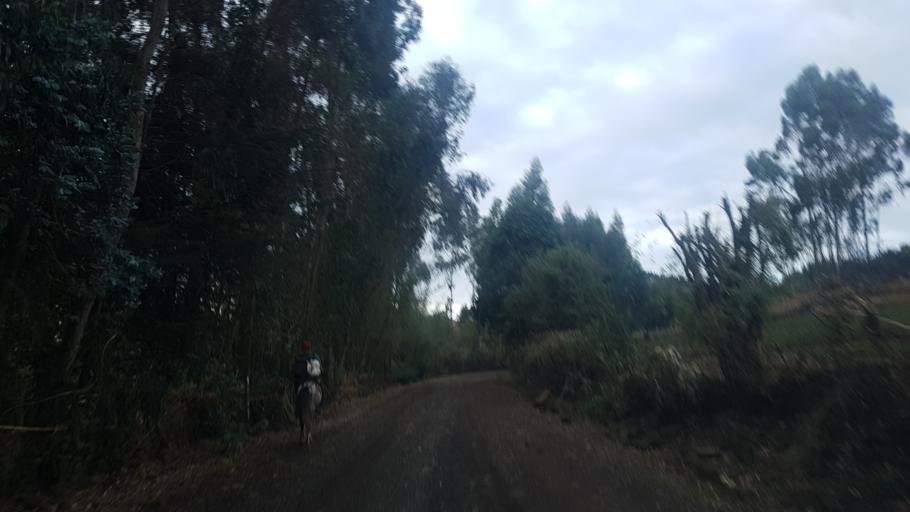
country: ET
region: Amhara
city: Finote Selam
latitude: 10.8012
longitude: 37.6634
